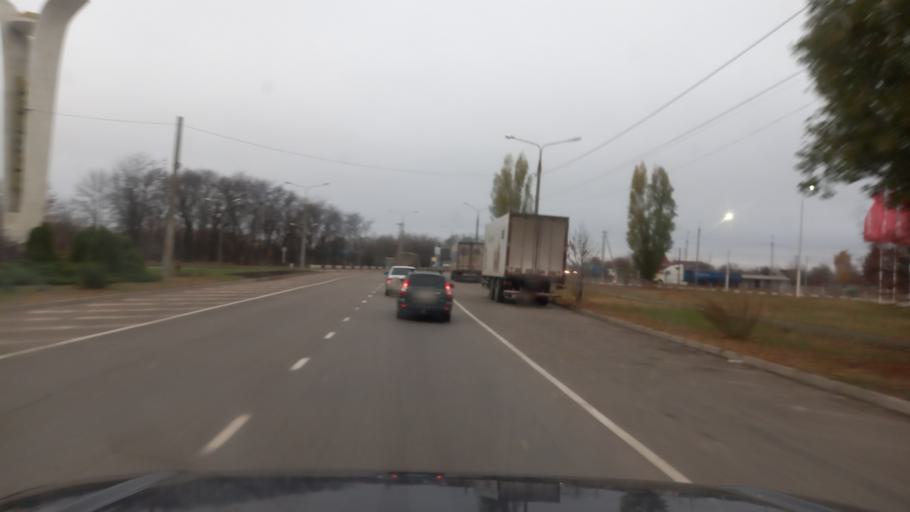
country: RU
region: Adygeya
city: Maykop
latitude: 44.6235
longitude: 40.0555
